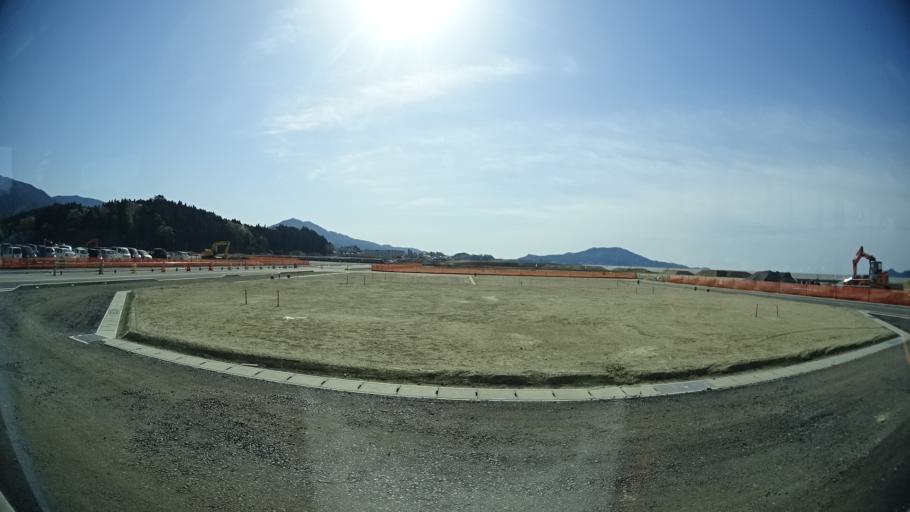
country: JP
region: Iwate
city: Ofunato
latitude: 39.0150
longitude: 141.6302
